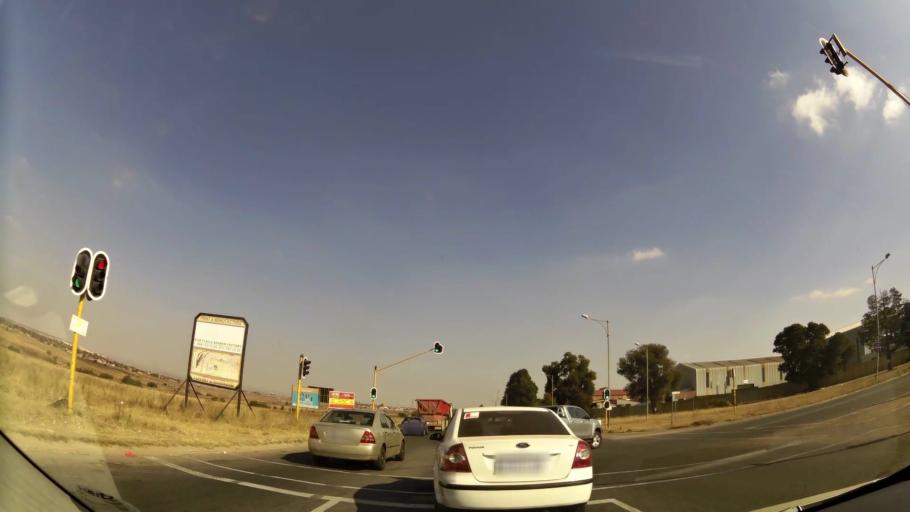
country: ZA
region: Gauteng
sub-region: City of Johannesburg Metropolitan Municipality
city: Roodepoort
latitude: -26.1476
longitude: 27.8132
